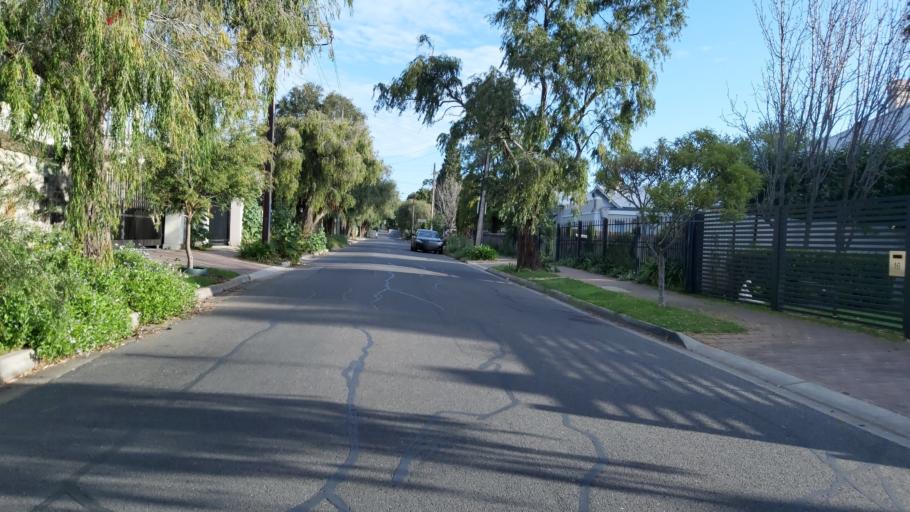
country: AU
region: South Australia
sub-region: Unley
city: Fullarton
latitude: -34.9518
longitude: 138.6288
